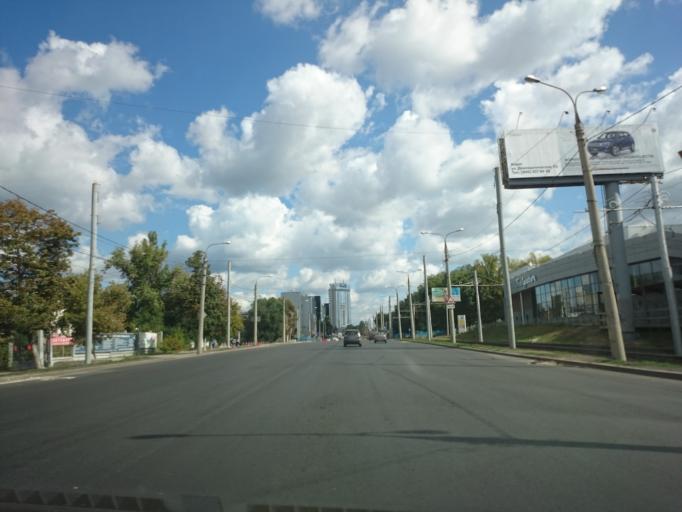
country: RU
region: Samara
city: Samara
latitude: 53.2145
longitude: 50.1447
